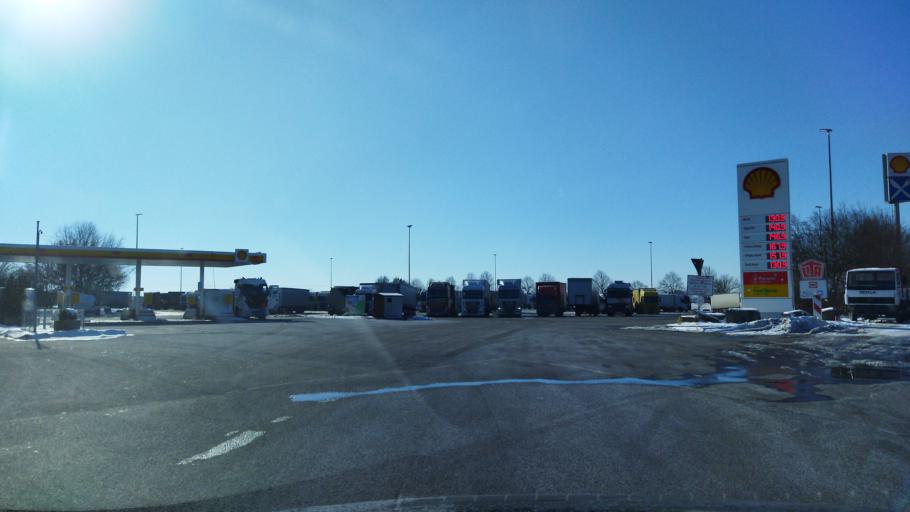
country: DE
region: Baden-Wuerttemberg
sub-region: Regierungsbezirk Stuttgart
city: Kirchberg an der Jagst
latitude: 49.1720
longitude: 9.9623
